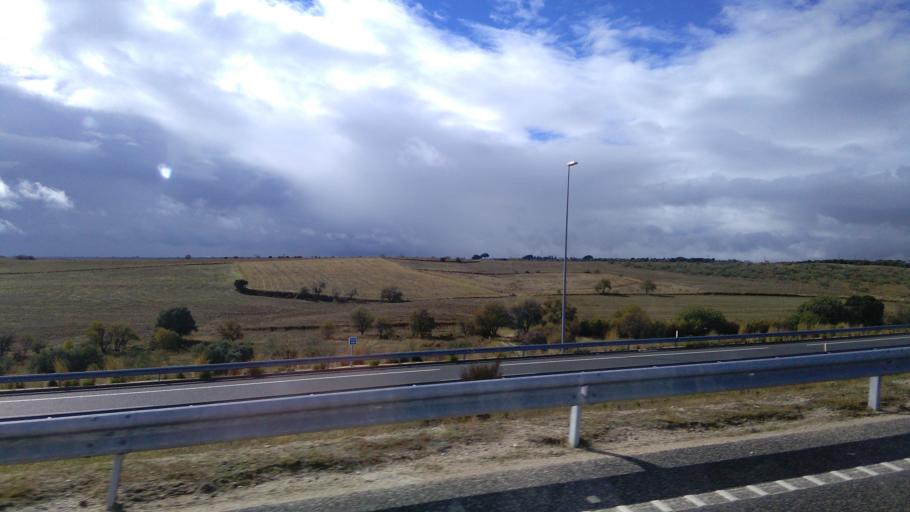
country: ES
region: Madrid
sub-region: Provincia de Madrid
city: Navalcarnero
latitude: 40.2665
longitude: -4.0312
